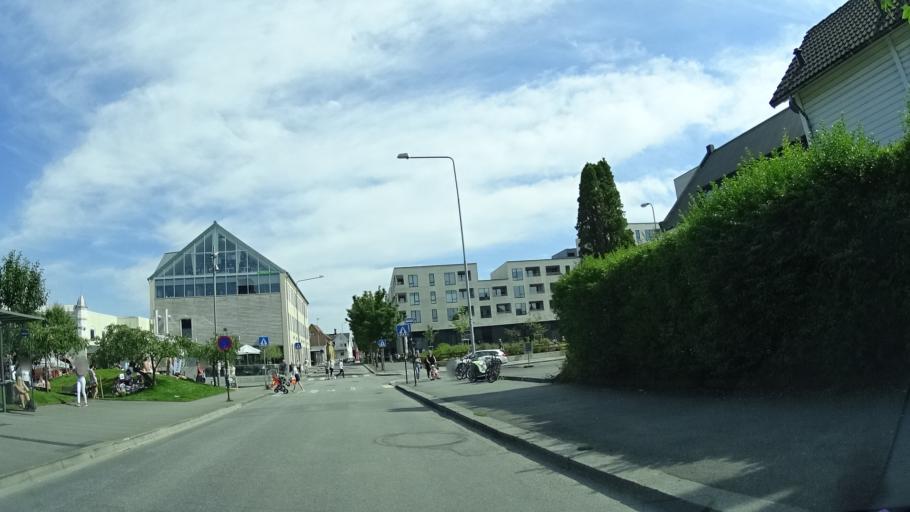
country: NO
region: Rogaland
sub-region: Stavanger
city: Stavanger
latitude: 58.9688
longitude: 5.7549
